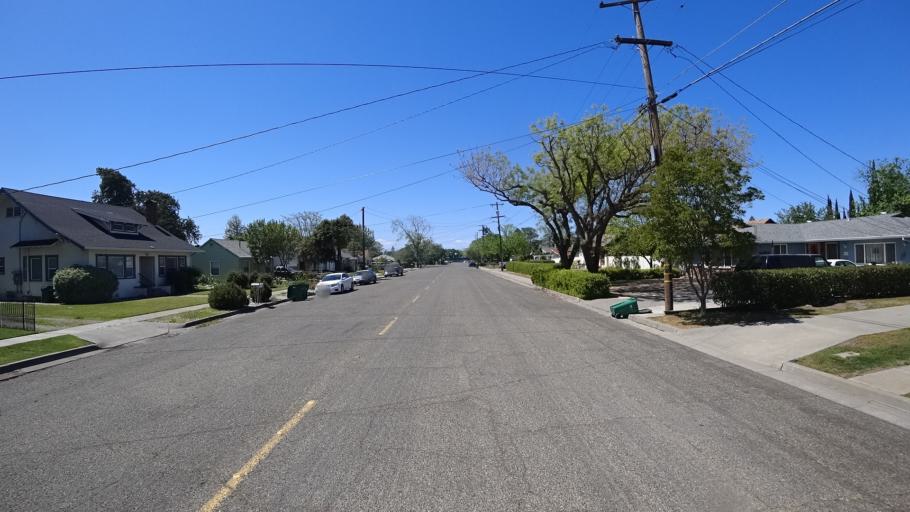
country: US
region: California
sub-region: Glenn County
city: Orland
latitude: 39.7451
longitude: -122.1857
